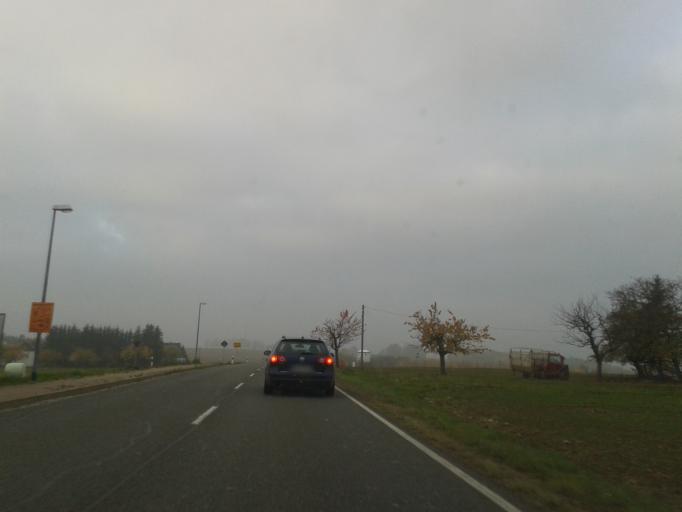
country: DE
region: Saxony
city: Niederschona
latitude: 50.9779
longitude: 13.4431
